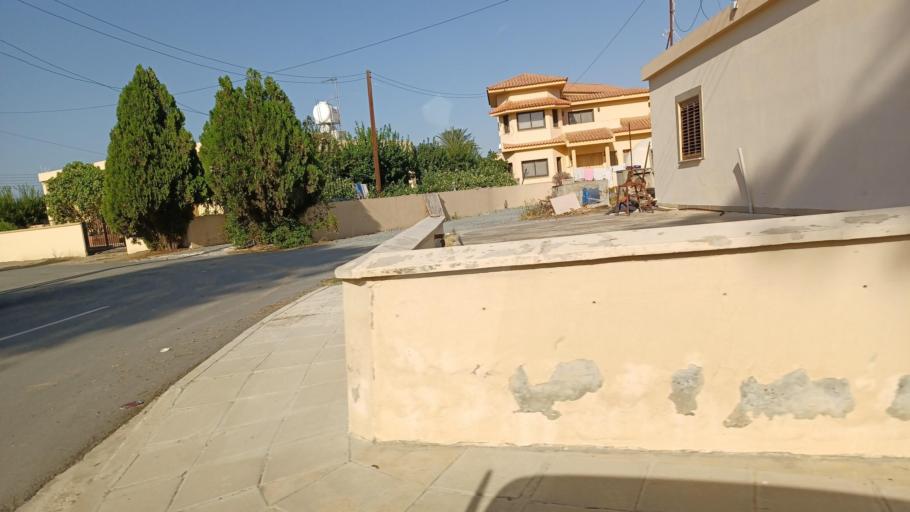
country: CY
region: Lefkosia
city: Alampra
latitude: 34.9935
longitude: 33.3670
